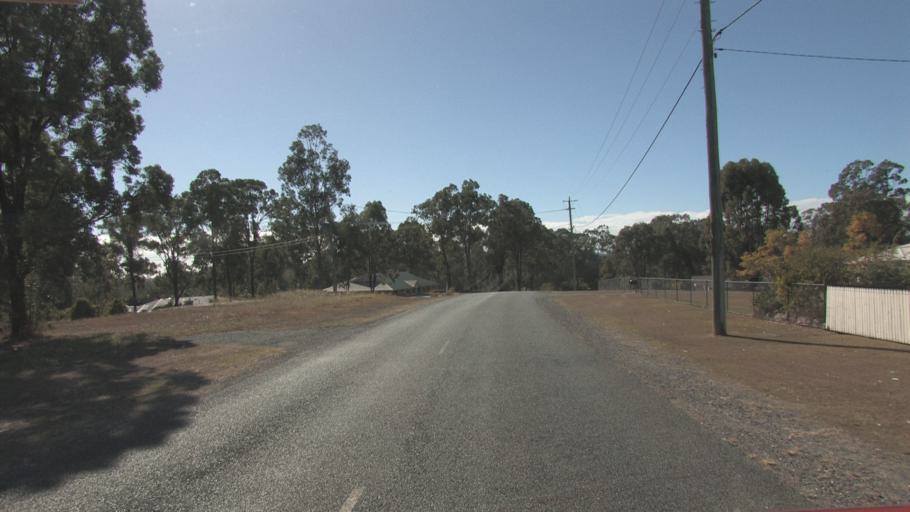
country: AU
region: Queensland
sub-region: Logan
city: Cedar Vale
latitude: -27.8807
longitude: 153.0061
